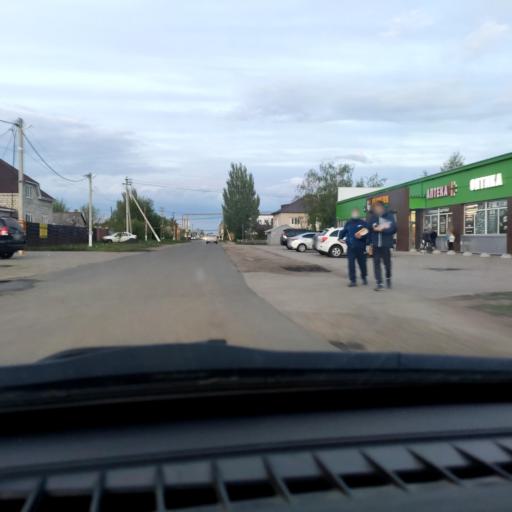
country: RU
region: Samara
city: Podstepki
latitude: 53.5166
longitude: 49.1151
